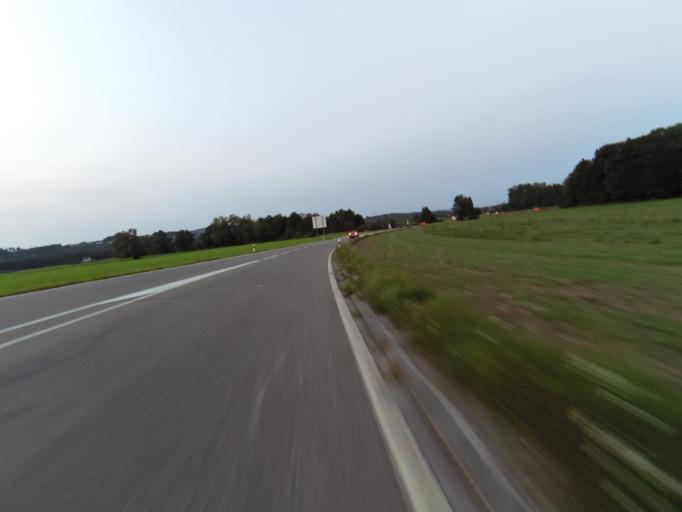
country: CH
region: Thurgau
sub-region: Frauenfeld District
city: Frauenfeld
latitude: 47.5655
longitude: 8.8716
